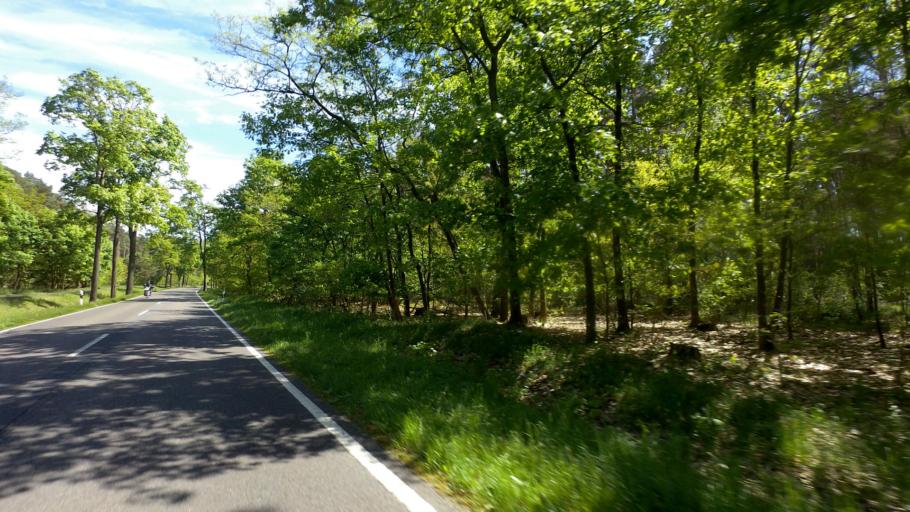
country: DE
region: Brandenburg
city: Sperenberg
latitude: 52.0482
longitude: 13.2984
